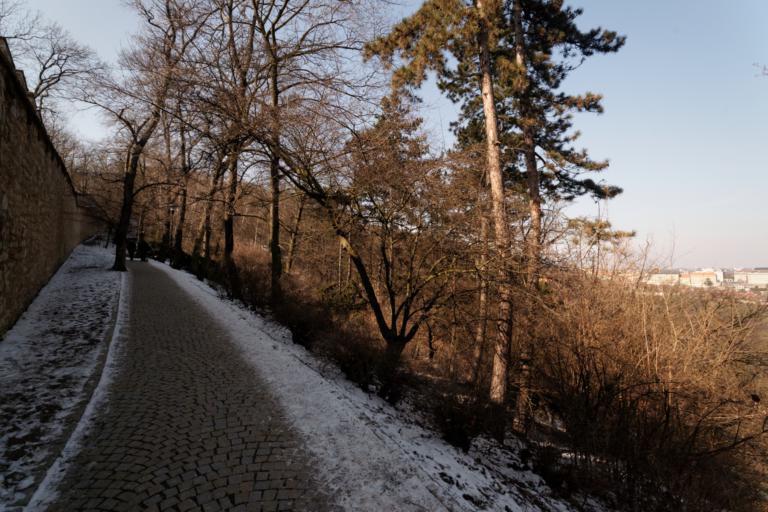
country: CZ
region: Praha
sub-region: Praha 1
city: Mala Strana
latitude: 50.0808
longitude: 14.4018
